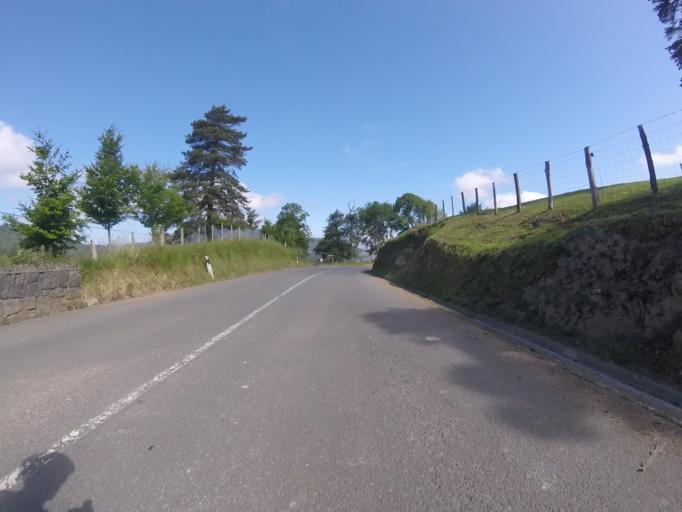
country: ES
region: Basque Country
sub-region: Provincia de Guipuzcoa
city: Ormaiztegui
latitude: 43.0875
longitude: -2.2455
